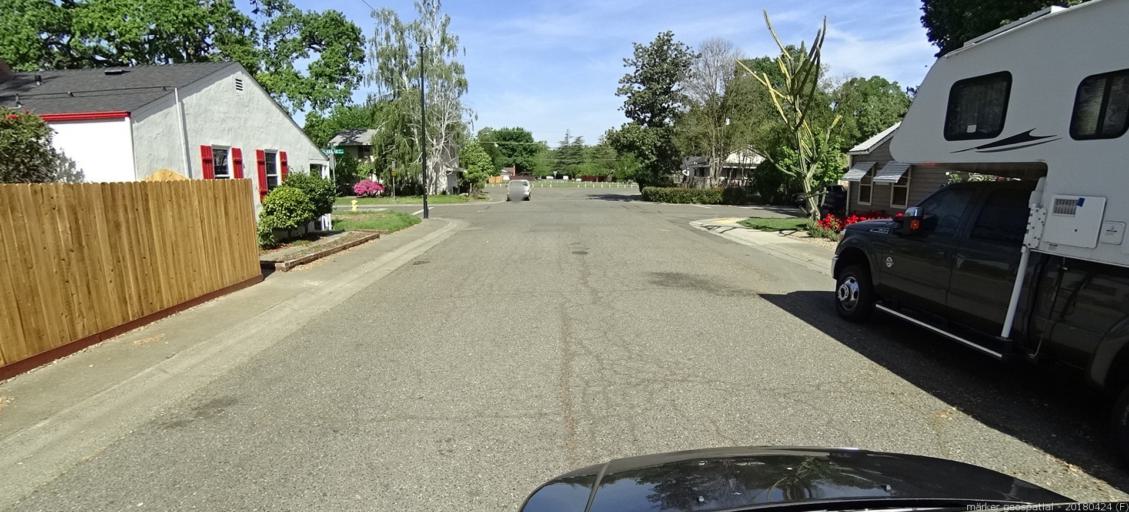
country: US
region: California
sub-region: Yolo County
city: West Sacramento
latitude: 38.5661
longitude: -121.5294
